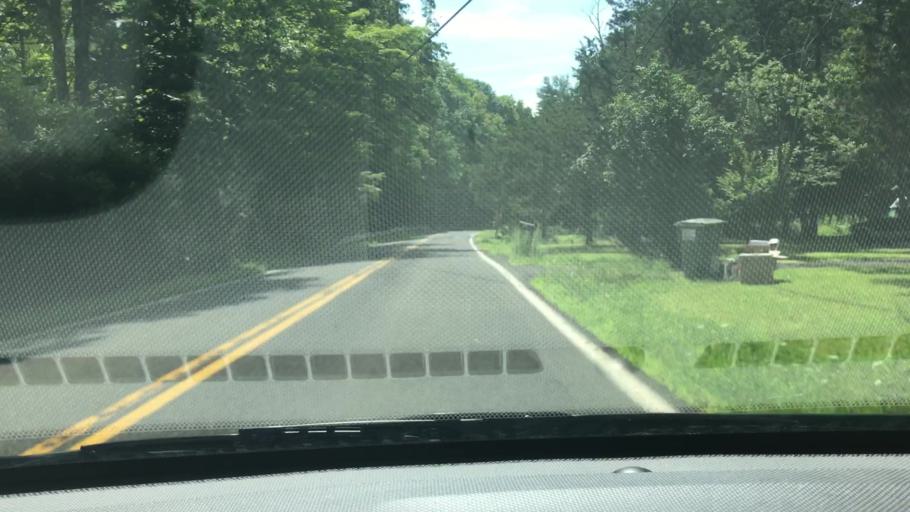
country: US
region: New York
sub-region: Ulster County
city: Stone Ridge
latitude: 41.9024
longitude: -74.1694
